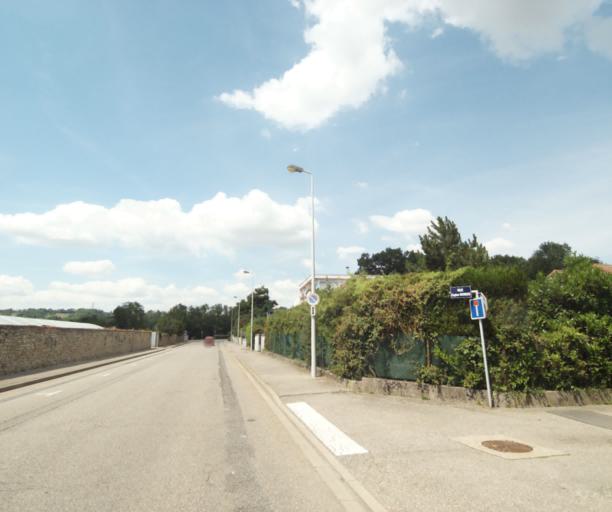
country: FR
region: Lorraine
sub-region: Departement de Meurthe-et-Moselle
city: Luneville
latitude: 48.5926
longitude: 6.4869
